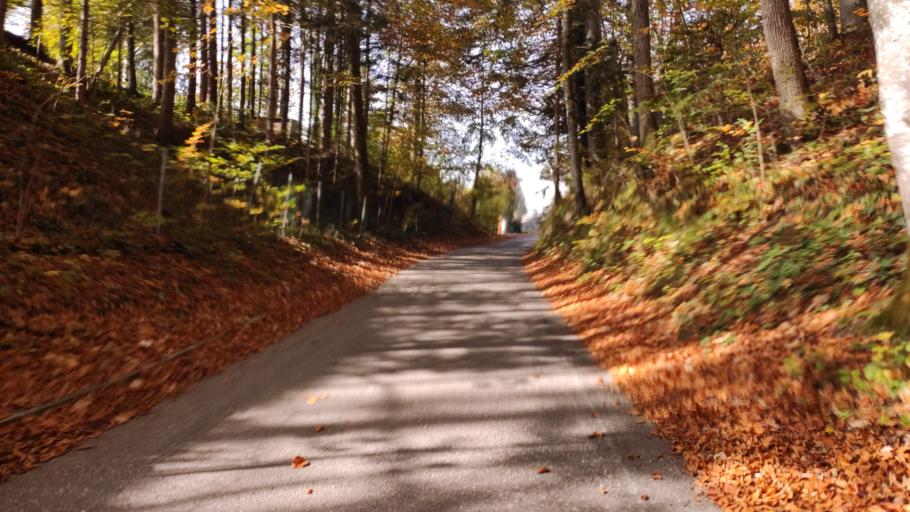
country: AT
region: Salzburg
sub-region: Politischer Bezirk Salzburg-Umgebung
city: Strobl
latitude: 47.7191
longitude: 13.5260
